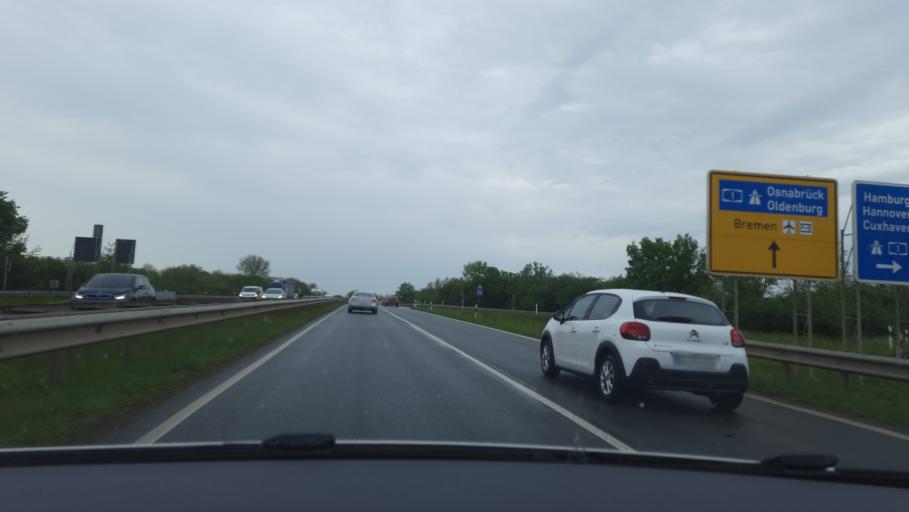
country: DE
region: Bremen
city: Bremen
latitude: 53.0277
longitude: 8.8600
